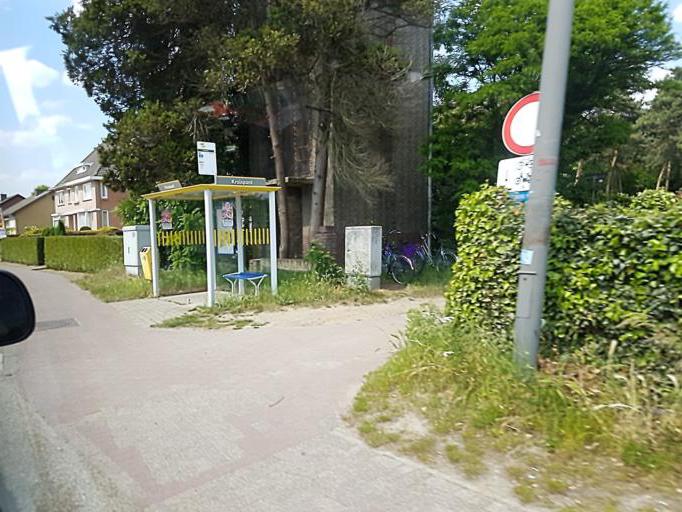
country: BE
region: Flanders
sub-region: Provincie Limburg
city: Bocholt
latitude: 51.1921
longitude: 5.5146
